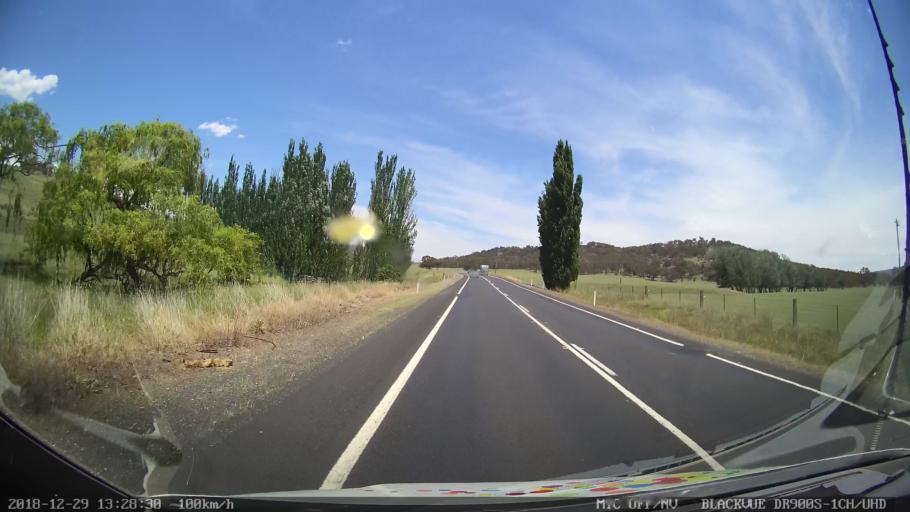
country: AU
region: New South Wales
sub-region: Cooma-Monaro
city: Cooma
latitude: -35.8767
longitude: 149.1609
